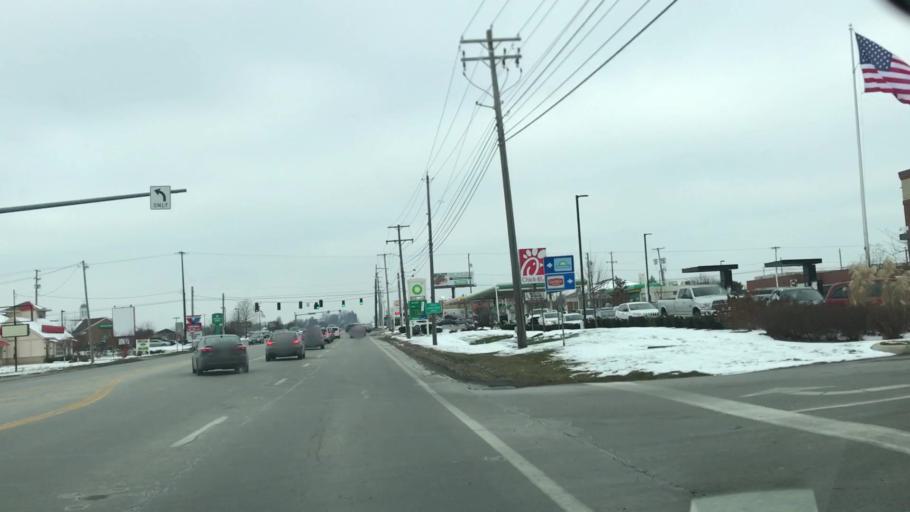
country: US
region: Ohio
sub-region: Mahoning County
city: Poland
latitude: 41.0244
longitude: -80.6325
